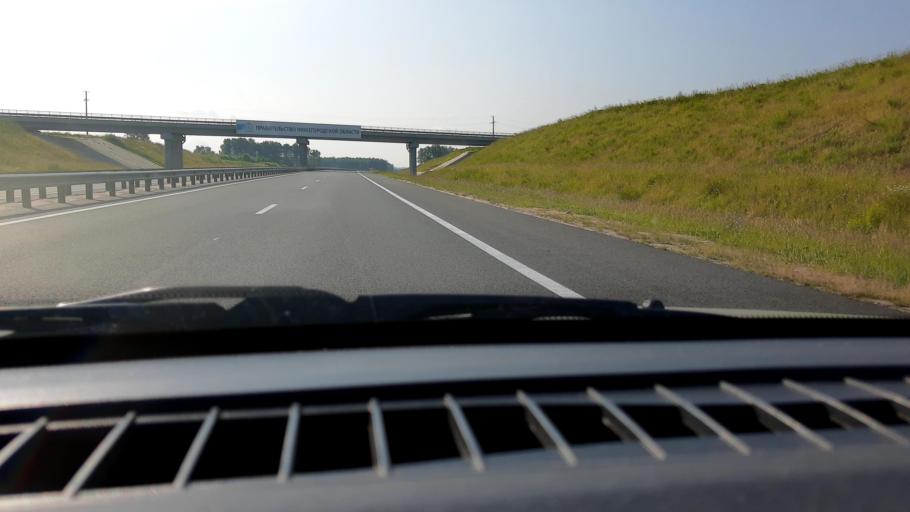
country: RU
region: Nizjnij Novgorod
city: Kstovo
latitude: 56.0931
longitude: 44.0779
